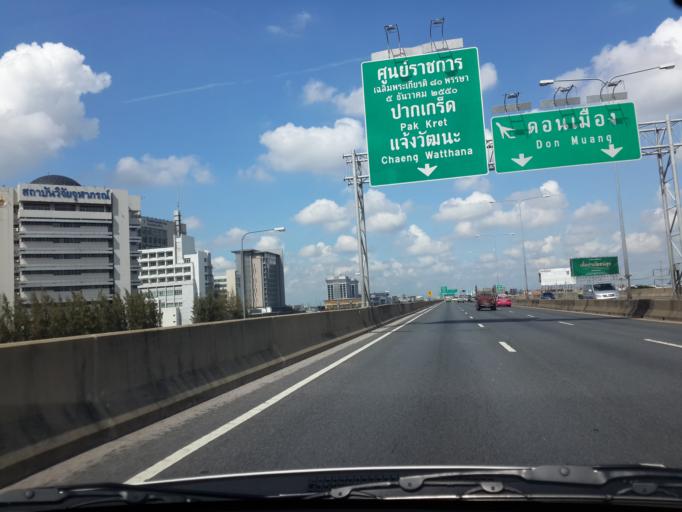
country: TH
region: Bangkok
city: Lak Si
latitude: 13.8778
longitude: 100.5779
